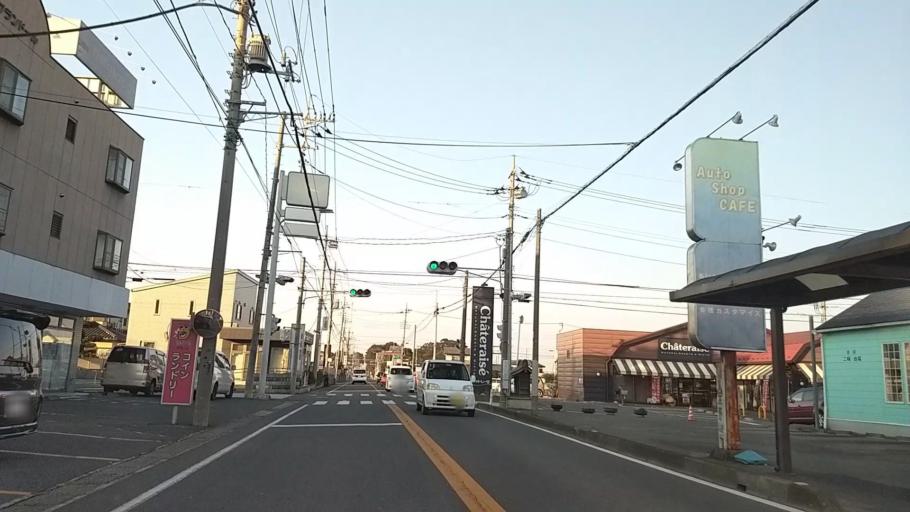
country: JP
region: Saitama
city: Tokorozawa
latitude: 35.8204
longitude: 139.4655
